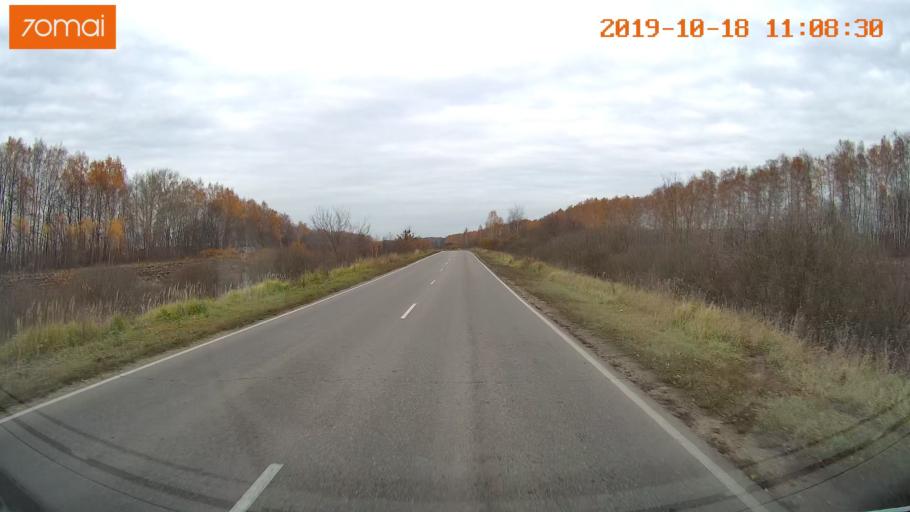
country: RU
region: Tula
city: Kimovsk
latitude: 53.9391
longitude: 38.5369
